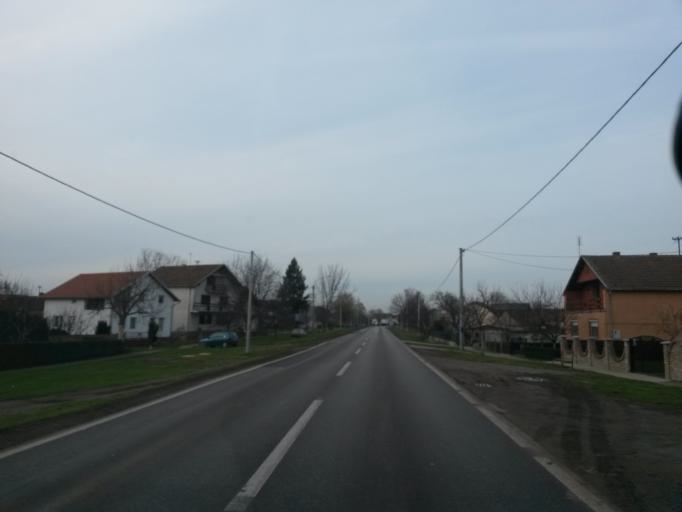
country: HR
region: Vukovarsko-Srijemska
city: Trpinja
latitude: 45.4081
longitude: 18.9079
